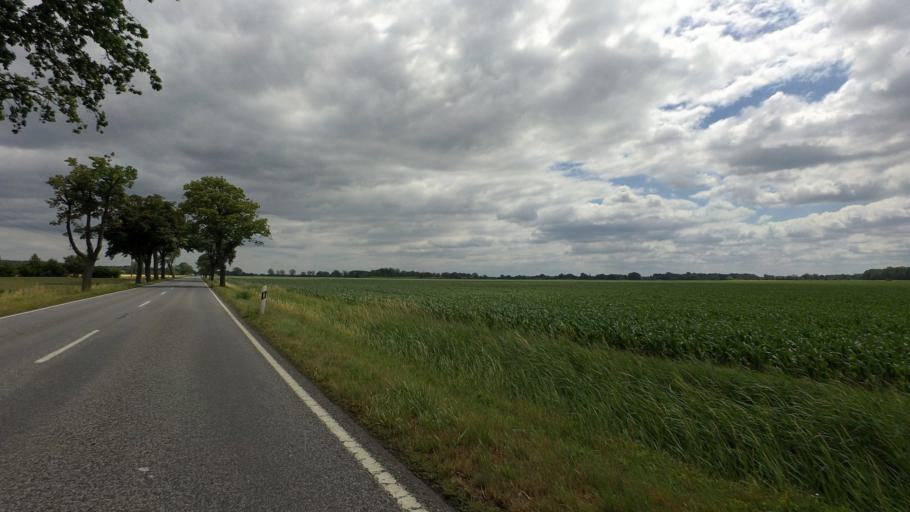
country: DE
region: Brandenburg
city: Luckau
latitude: 51.8390
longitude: 13.7556
